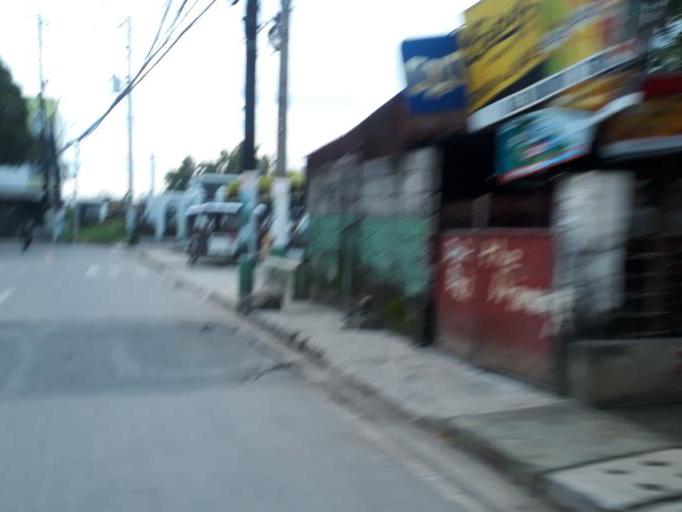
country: PH
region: Central Luzon
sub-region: Province of Bulacan
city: Obando
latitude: 14.7108
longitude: 120.9511
